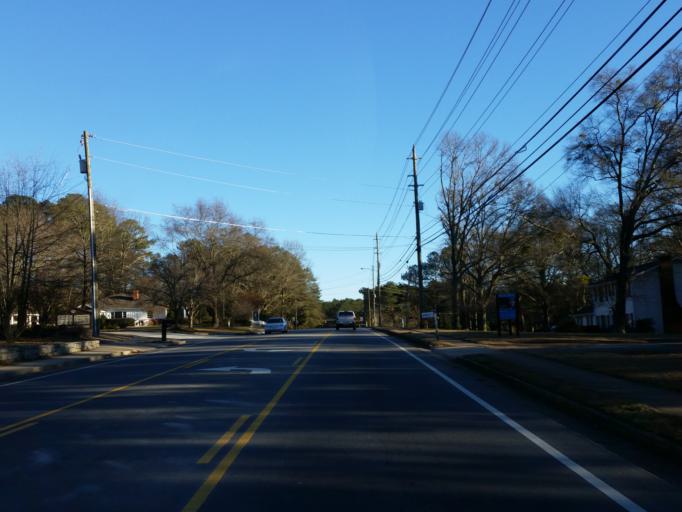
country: US
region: Georgia
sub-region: Cobb County
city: Kennesaw
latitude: 33.9652
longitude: -84.6627
